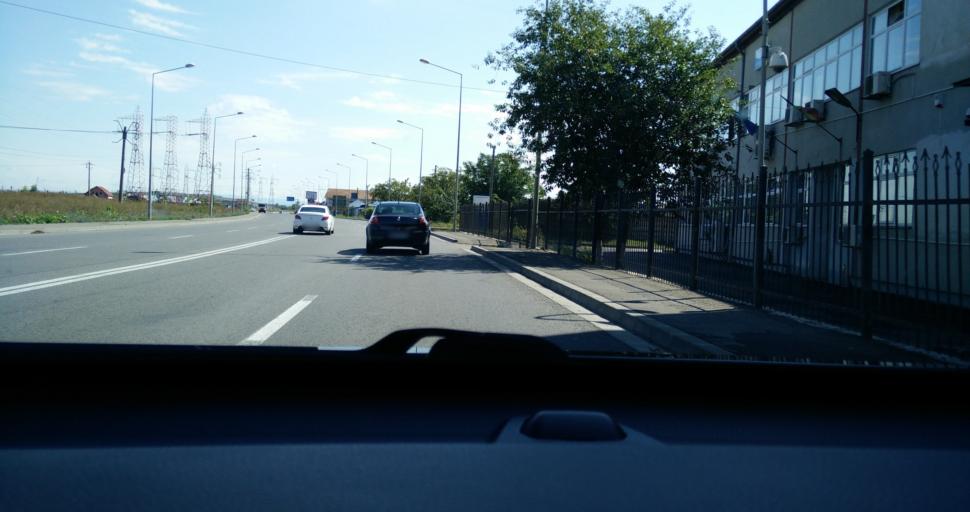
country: RO
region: Bihor
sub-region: Comuna Sanmartin
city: Sanmartin
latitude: 47.0303
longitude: 21.9860
